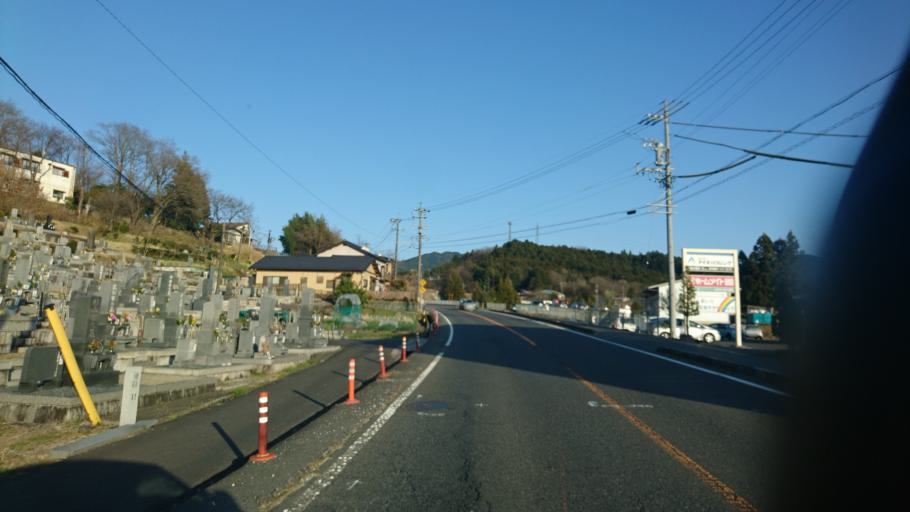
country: JP
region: Gifu
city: Nakatsugawa
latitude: 35.4537
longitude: 137.4224
